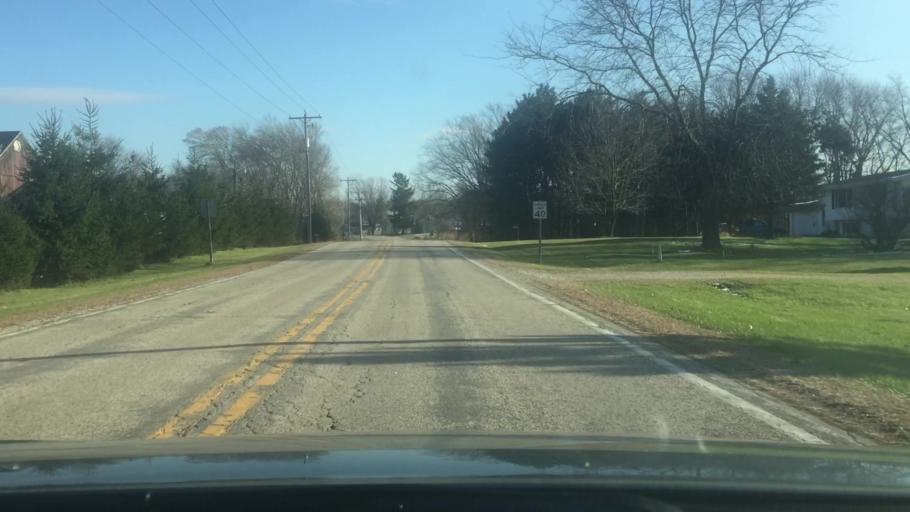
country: US
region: Wisconsin
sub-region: Jefferson County
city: Palmyra
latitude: 42.9382
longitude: -88.5898
